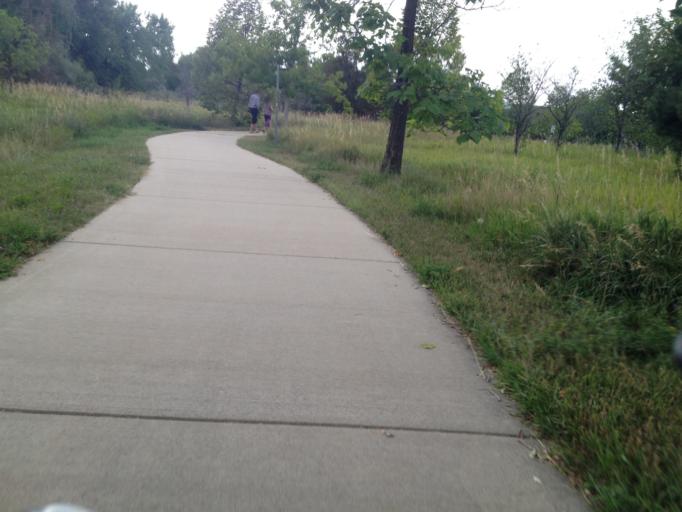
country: US
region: Colorado
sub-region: Boulder County
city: Louisville
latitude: 39.9897
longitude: -105.1583
